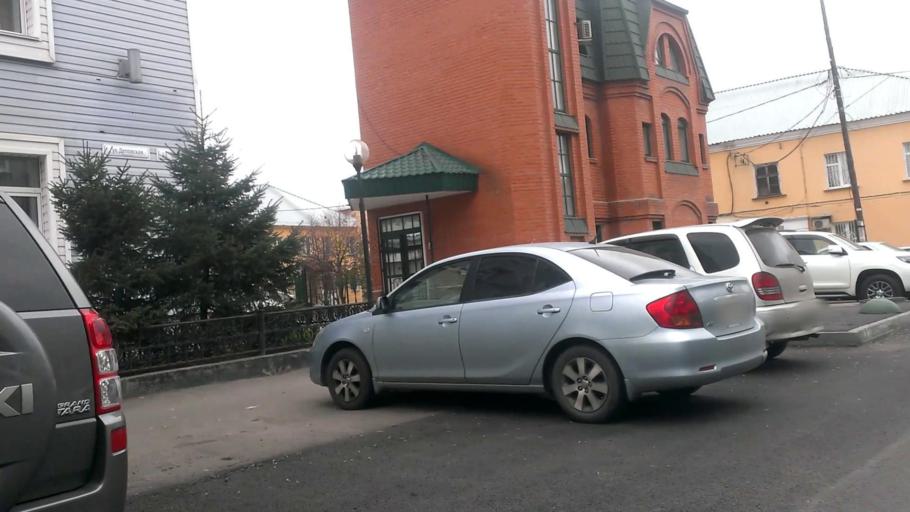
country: RU
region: Altai Krai
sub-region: Gorod Barnaulskiy
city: Barnaul
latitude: 53.3528
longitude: 83.7678
